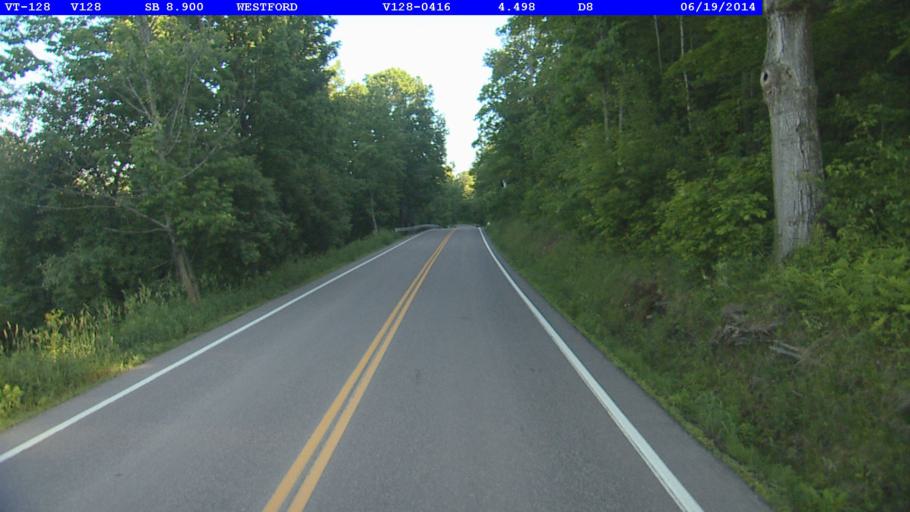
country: US
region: Vermont
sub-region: Chittenden County
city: Milton
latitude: 44.6191
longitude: -73.0156
